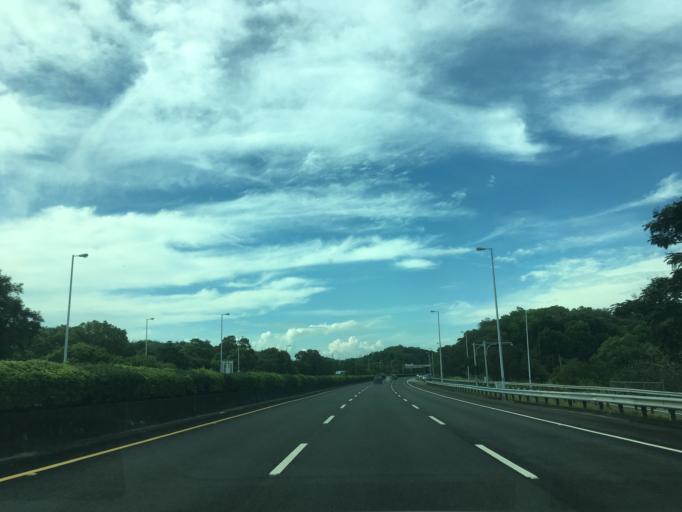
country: TW
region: Taiwan
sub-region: Chiayi
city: Jiayi Shi
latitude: 23.5217
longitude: 120.4848
